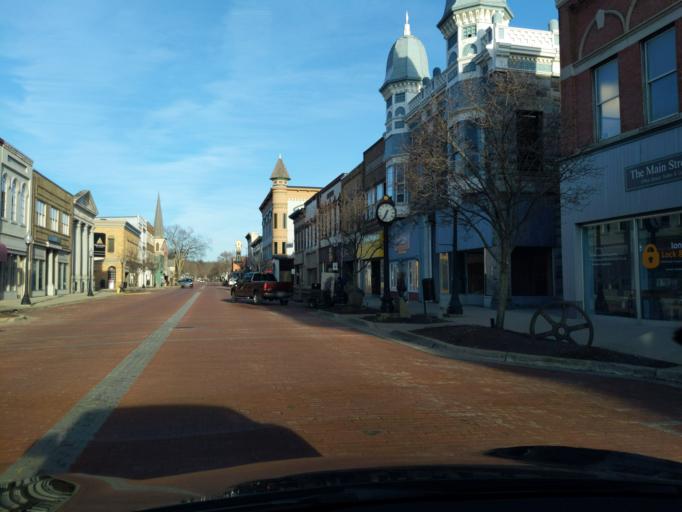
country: US
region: Michigan
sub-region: Ionia County
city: Ionia
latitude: 42.9825
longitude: -85.0667
